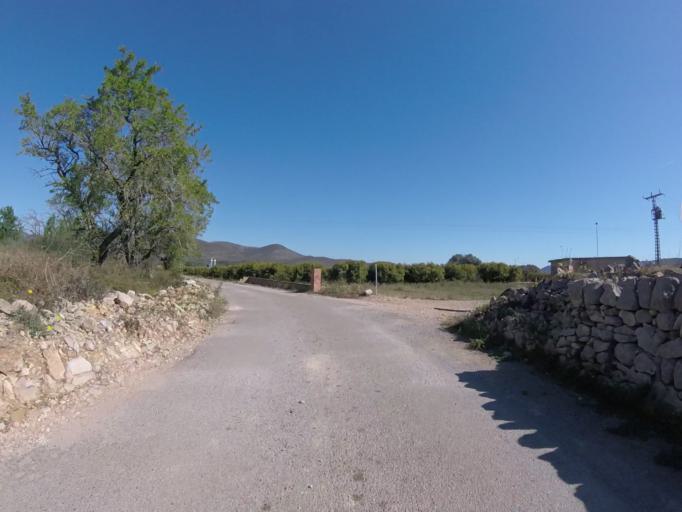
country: ES
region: Valencia
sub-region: Provincia de Castello
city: Santa Magdalena de Pulpis
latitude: 40.3578
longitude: 0.2858
